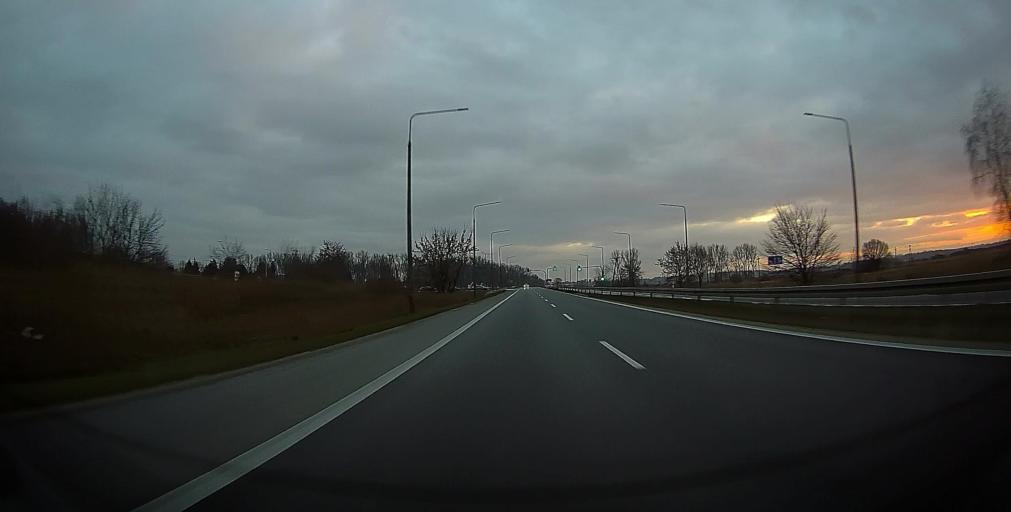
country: PL
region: Masovian Voivodeship
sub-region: Powiat radomski
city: Jedlinsk
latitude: 51.5105
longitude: 21.1168
